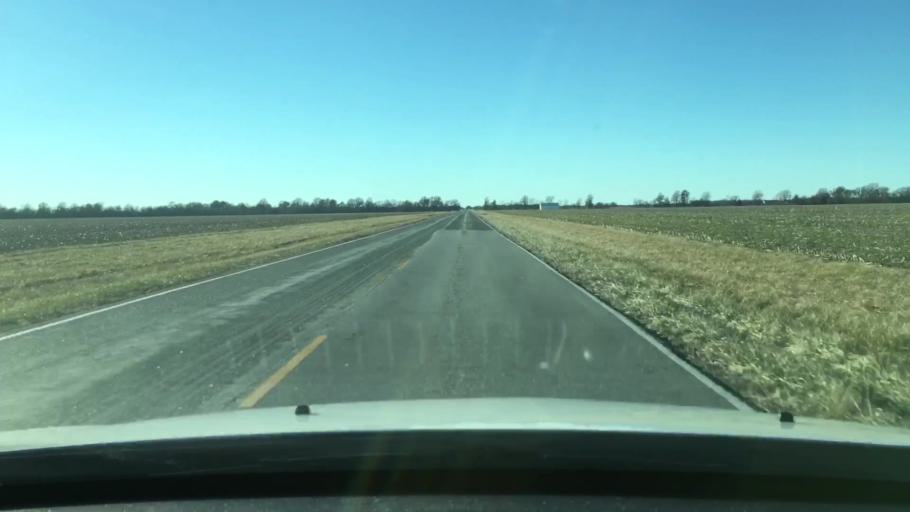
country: US
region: Missouri
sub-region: Audrain County
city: Vandalia
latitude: 39.2814
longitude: -91.6763
